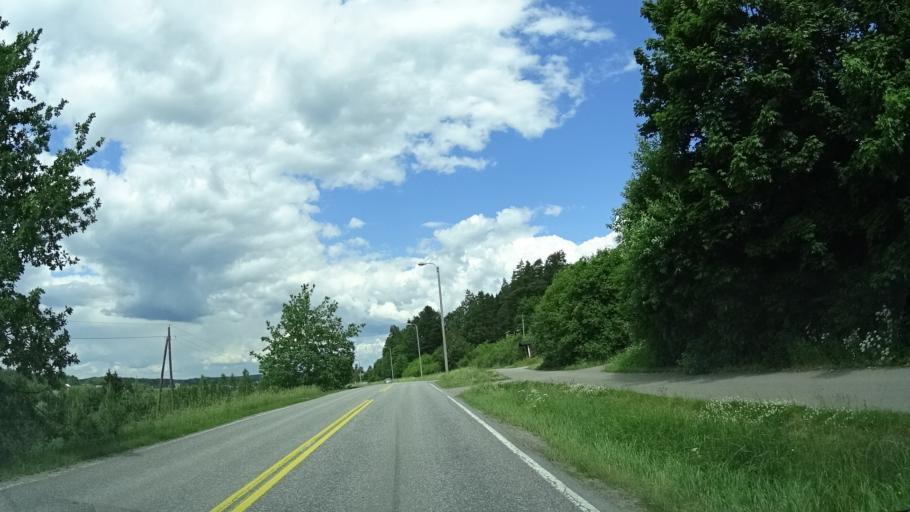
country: FI
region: Uusimaa
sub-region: Helsinki
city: Nurmijaervi
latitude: 60.3857
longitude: 24.6477
